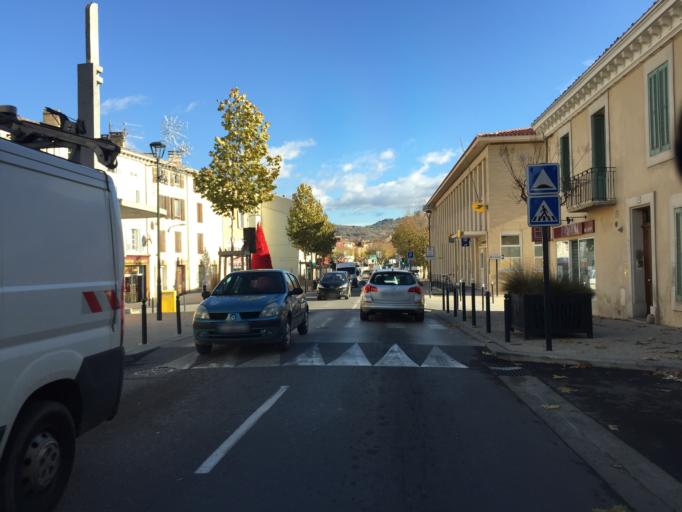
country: FR
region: Provence-Alpes-Cote d'Azur
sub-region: Departement du Vaucluse
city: Apt
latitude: 43.8774
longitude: 5.3910
